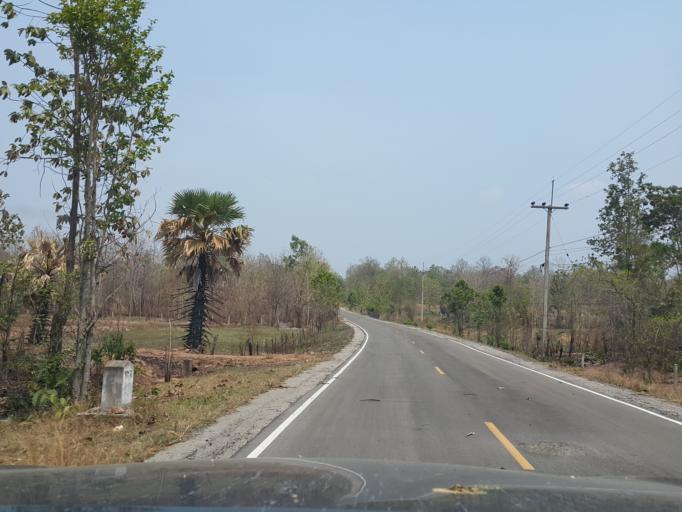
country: TH
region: Lampang
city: Mae Phrik
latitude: 17.5601
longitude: 99.0986
